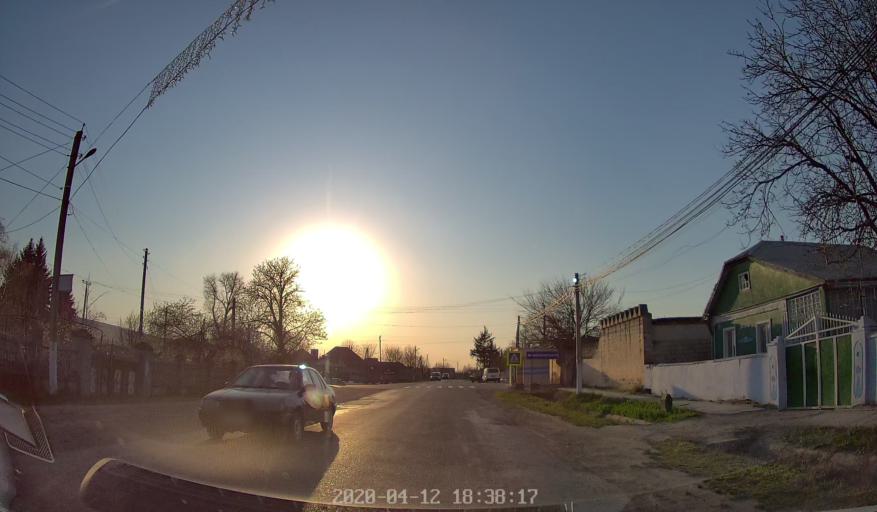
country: MD
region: Chisinau
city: Vadul lui Voda
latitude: 47.1239
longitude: 29.0026
